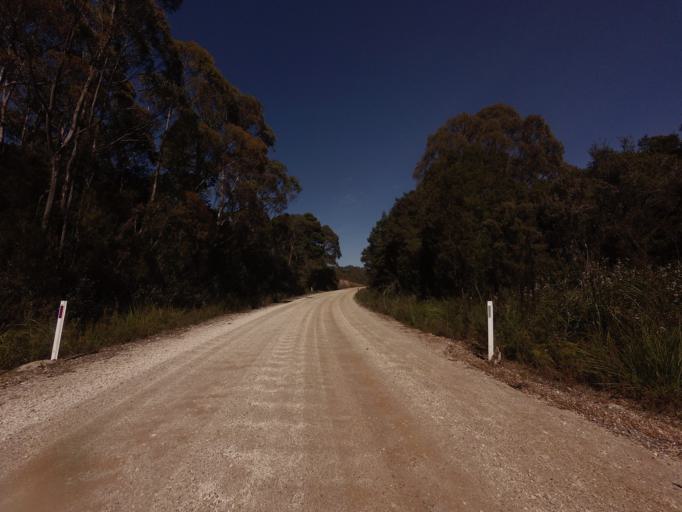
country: AU
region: Tasmania
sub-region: Huon Valley
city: Geeveston
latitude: -42.9953
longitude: 146.3701
